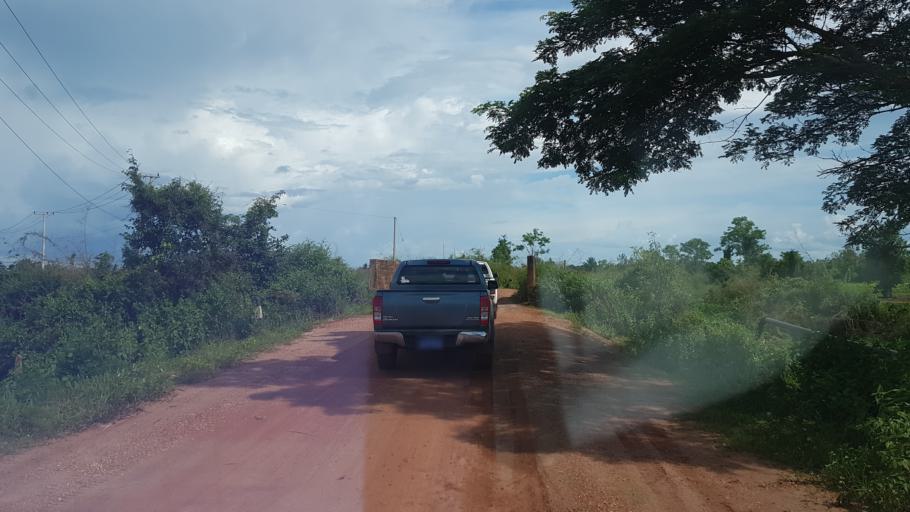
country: LA
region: Vientiane
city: Vientiane
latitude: 18.2091
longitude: 102.5660
